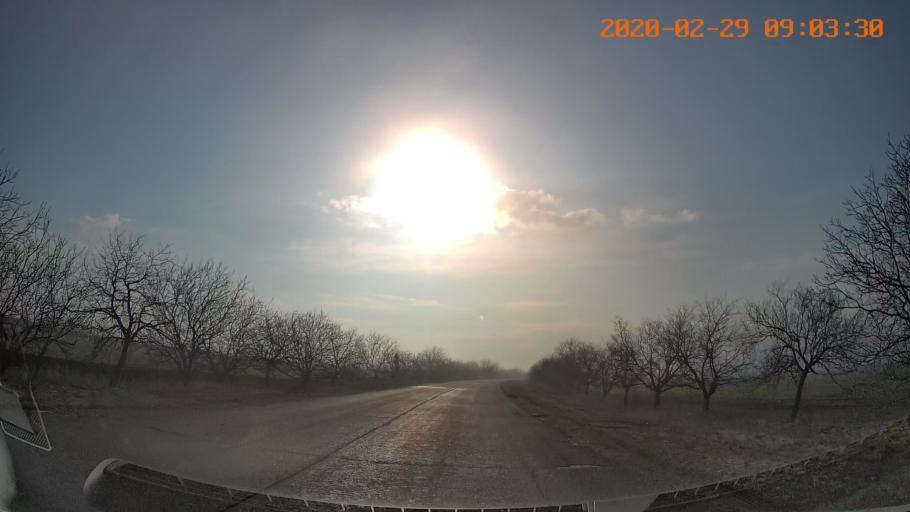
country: UA
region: Odessa
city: Velykoploske
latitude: 46.9152
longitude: 29.7296
